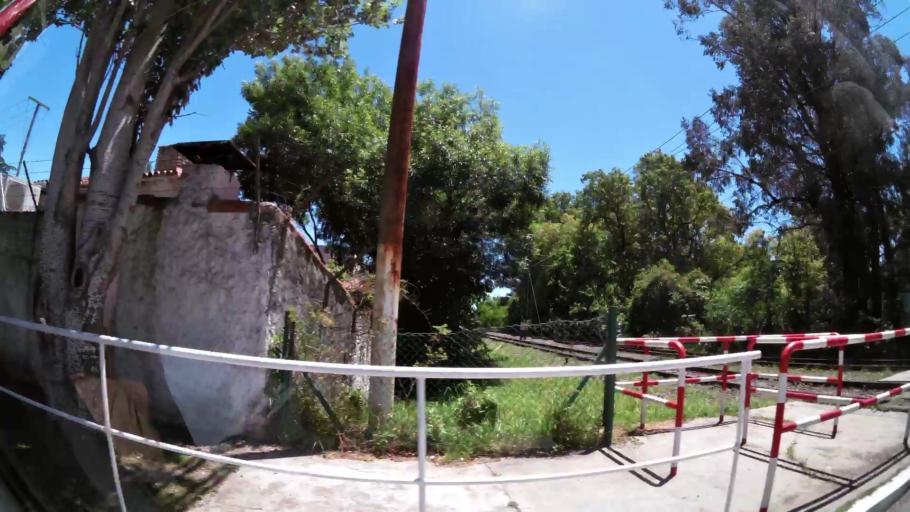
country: AR
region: Buenos Aires
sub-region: Partido de Tigre
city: Tigre
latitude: -34.4411
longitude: -58.5487
